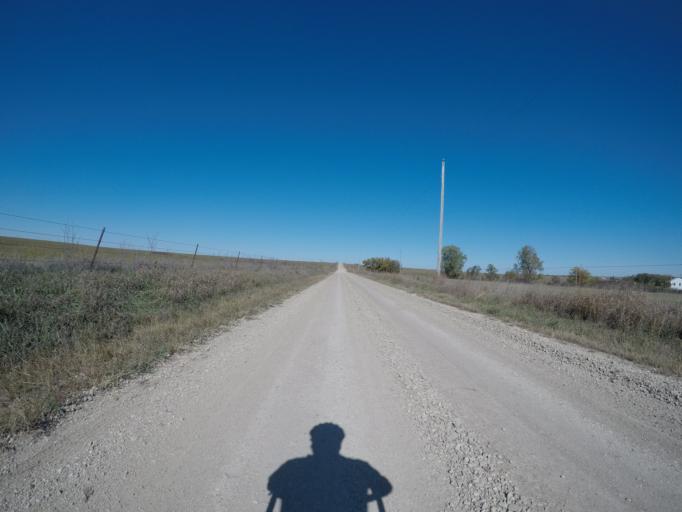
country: US
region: Kansas
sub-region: Wabaunsee County
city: Alma
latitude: 39.0374
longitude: -96.3722
